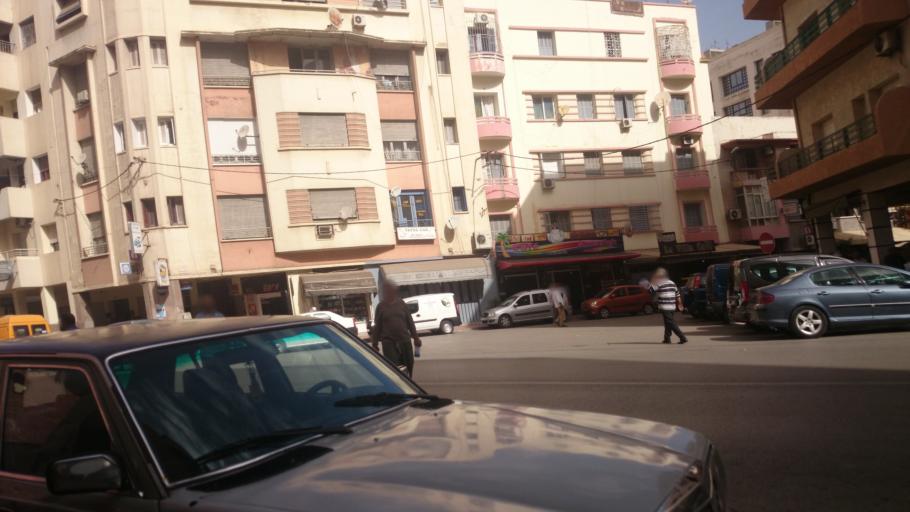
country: MA
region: Meknes-Tafilalet
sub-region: Meknes
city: Meknes
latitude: 33.8967
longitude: -5.5464
